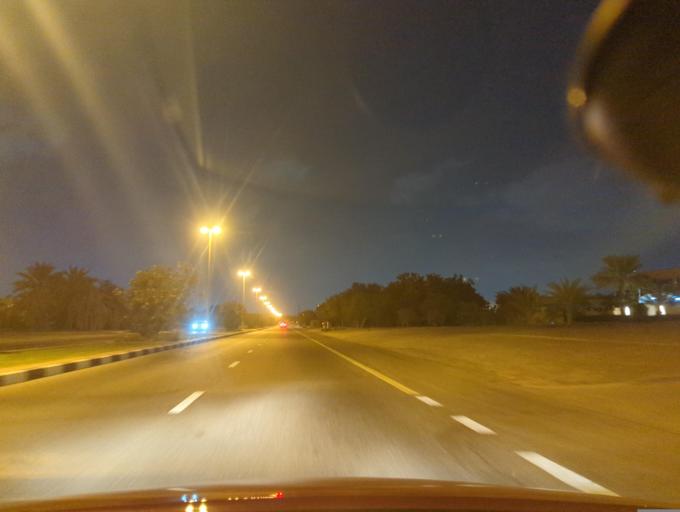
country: AE
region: Ash Shariqah
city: Sharjah
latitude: 25.3521
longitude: 55.4652
